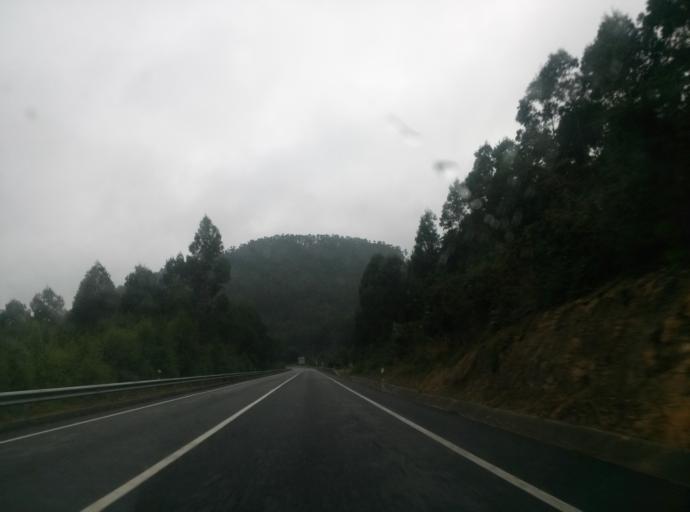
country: ES
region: Galicia
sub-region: Provincia de Lugo
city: Viveiro
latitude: 43.5693
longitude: -7.6432
